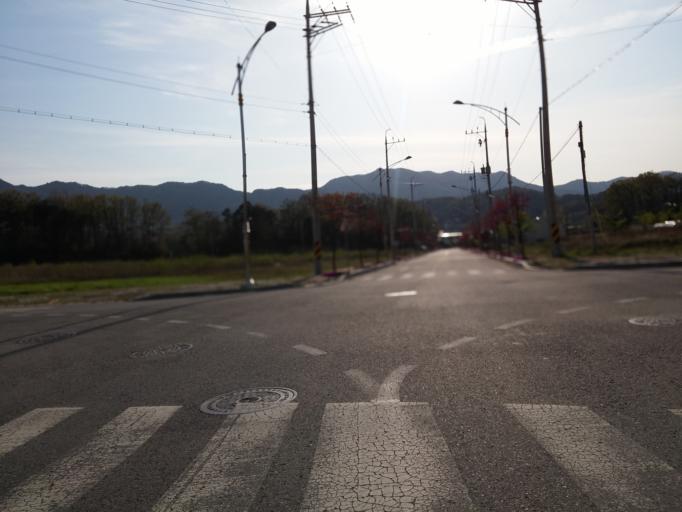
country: KR
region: Chungcheongbuk-do
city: Okcheon
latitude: 36.2738
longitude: 127.5915
